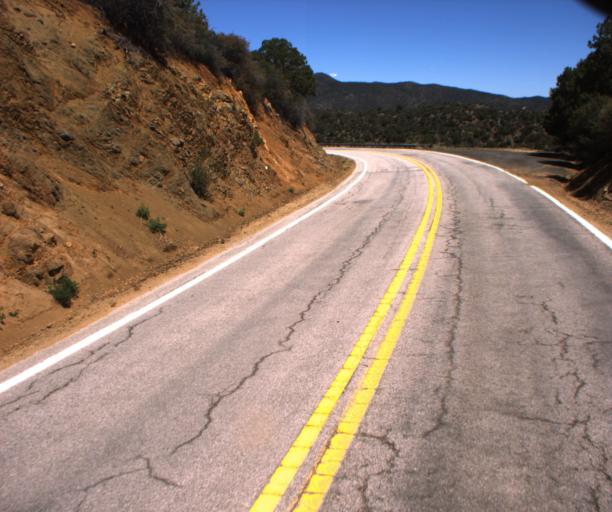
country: US
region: Arizona
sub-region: Yavapai County
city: Prescott
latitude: 34.4298
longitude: -112.5454
